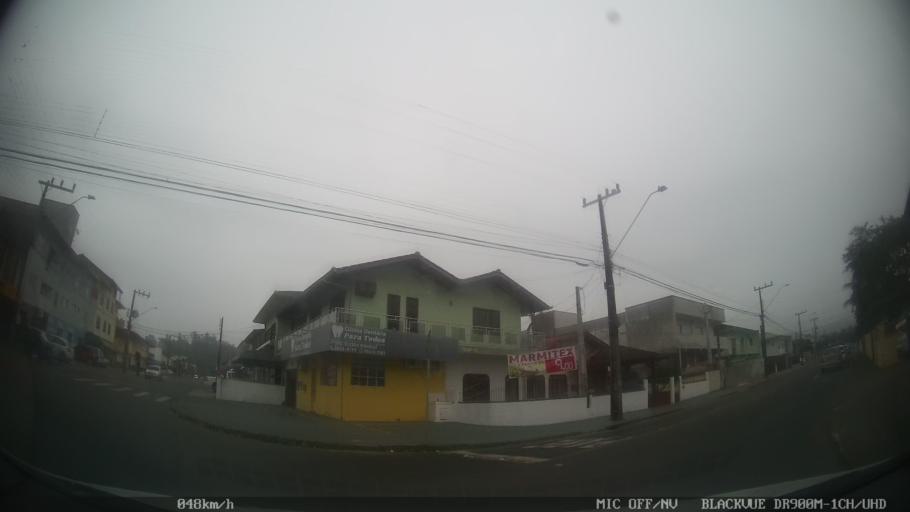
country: BR
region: Santa Catarina
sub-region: Joinville
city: Joinville
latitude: -26.2801
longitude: -48.8060
